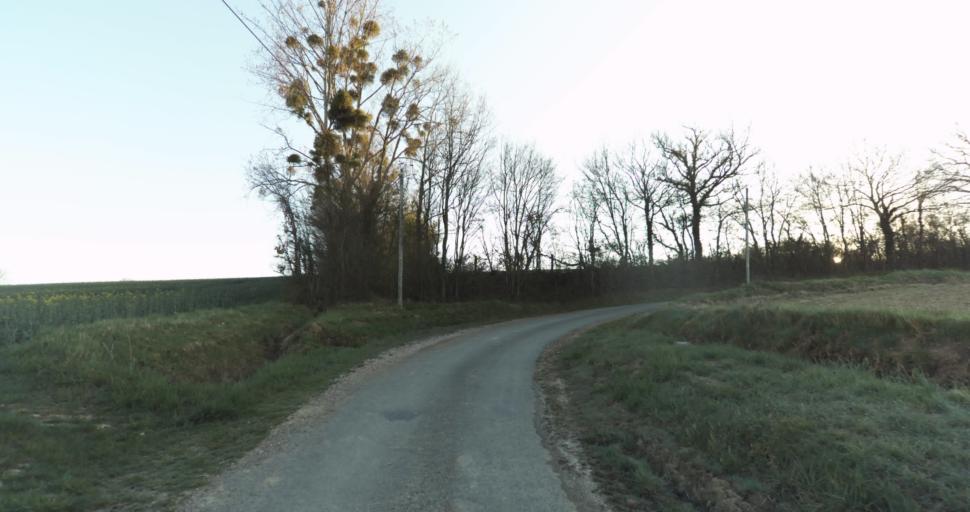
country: FR
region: Lower Normandy
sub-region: Departement du Calvados
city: Saint-Pierre-sur-Dives
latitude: 49.0253
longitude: 0.0001
